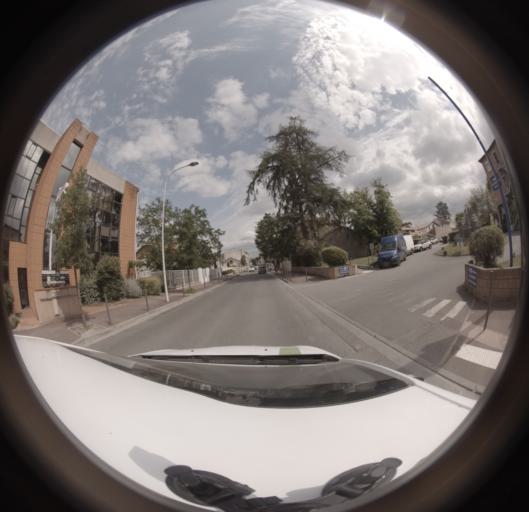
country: FR
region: Midi-Pyrenees
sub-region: Departement du Tarn-et-Garonne
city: Montauban
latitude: 44.0104
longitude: 1.3666
